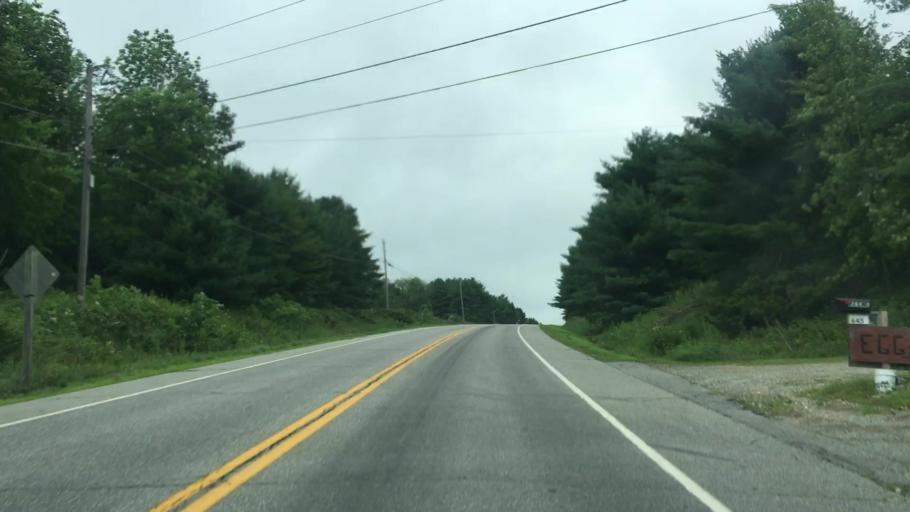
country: US
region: Maine
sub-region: Sagadahoc County
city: Richmond
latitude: 44.1124
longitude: -69.7311
